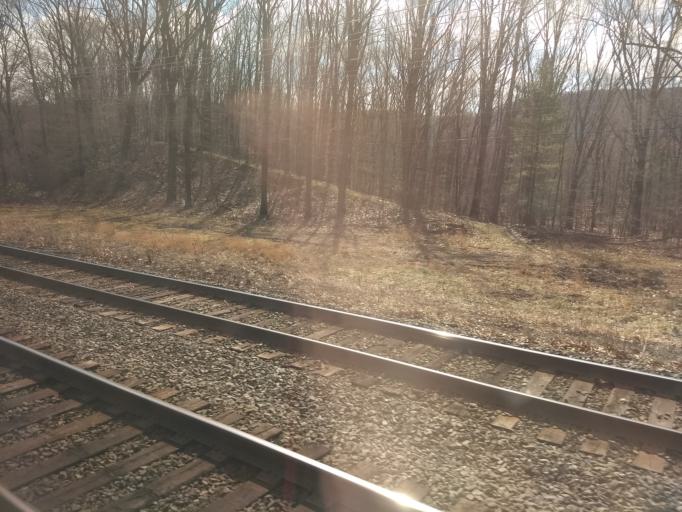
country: US
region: Pennsylvania
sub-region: Blair County
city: Tipton
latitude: 40.6342
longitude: -78.3001
